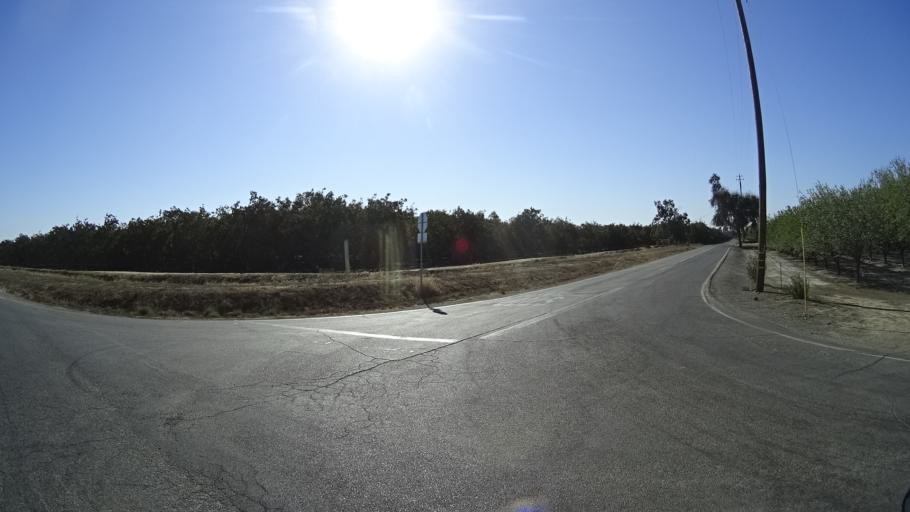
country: US
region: California
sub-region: Yolo County
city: Woodland
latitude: 38.7056
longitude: -121.8622
